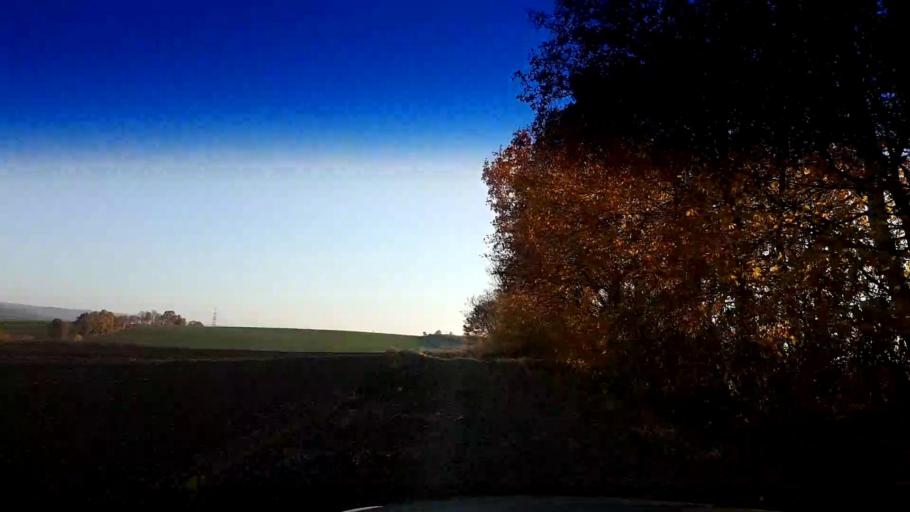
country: DE
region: Bavaria
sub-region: Upper Franconia
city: Memmelsdorf
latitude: 49.9715
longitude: 10.9721
